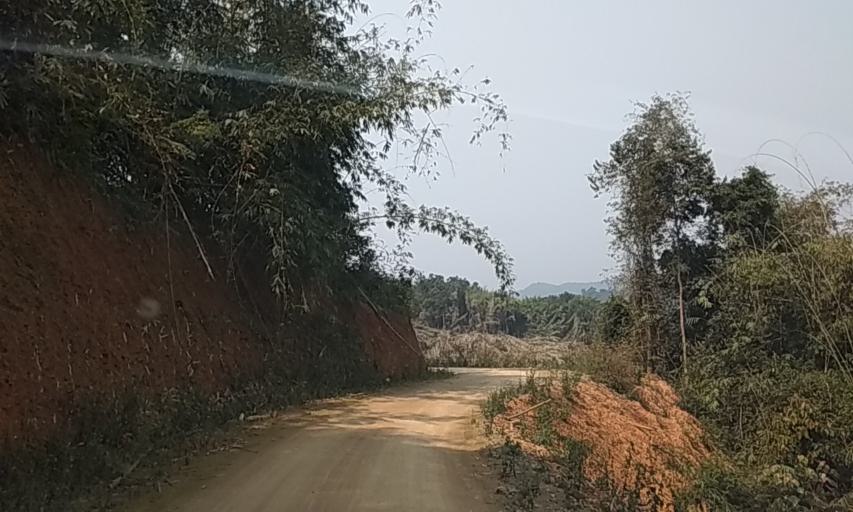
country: LA
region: Phongsali
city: Phongsali
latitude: 21.4705
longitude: 102.4266
